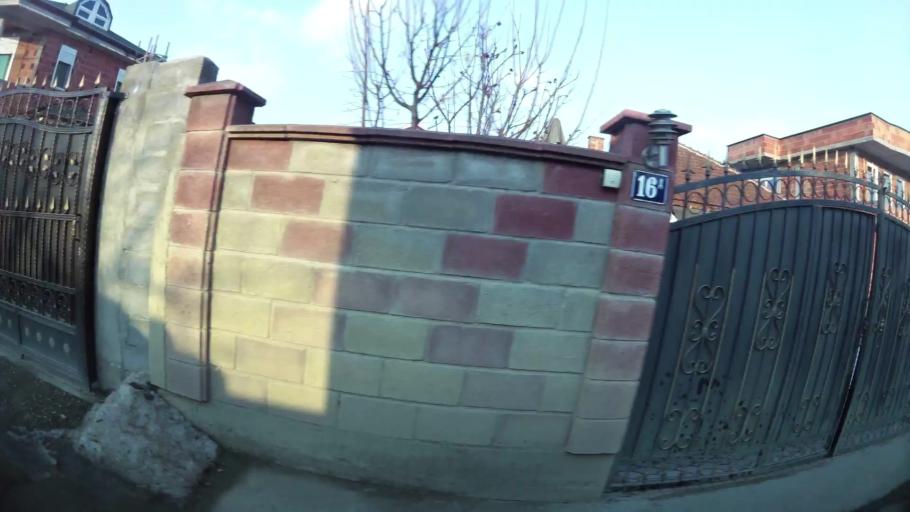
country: MK
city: Creshevo
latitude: 42.0179
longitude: 21.5209
